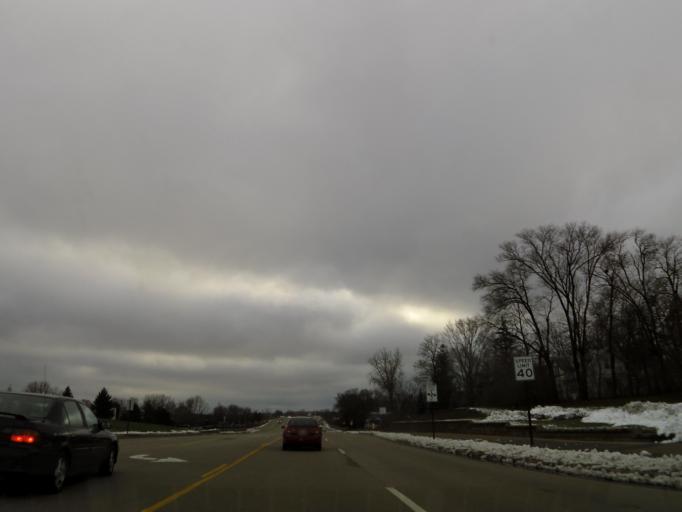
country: US
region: Minnesota
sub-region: Hennepin County
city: Minnetonka Mills
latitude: 44.9198
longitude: -93.4272
